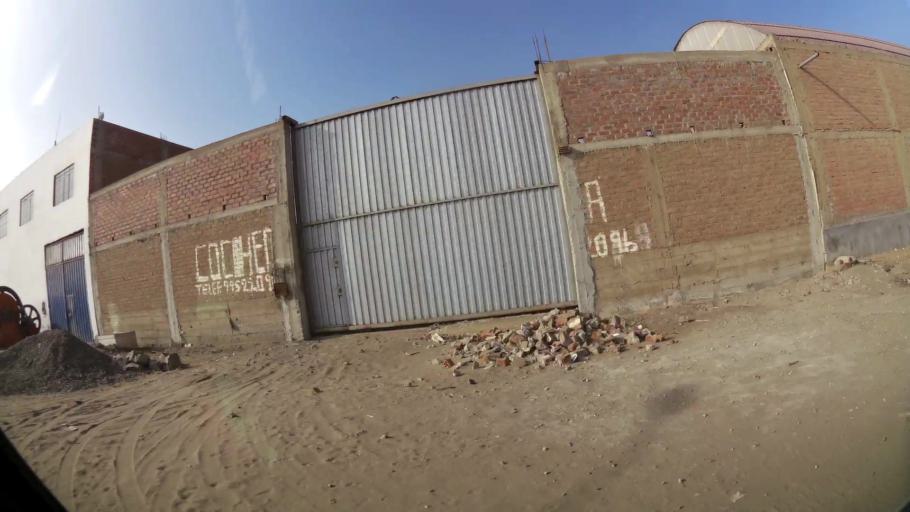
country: PE
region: Lima
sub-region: Lima
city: Santa Rosa
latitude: -11.7604
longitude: -77.1612
